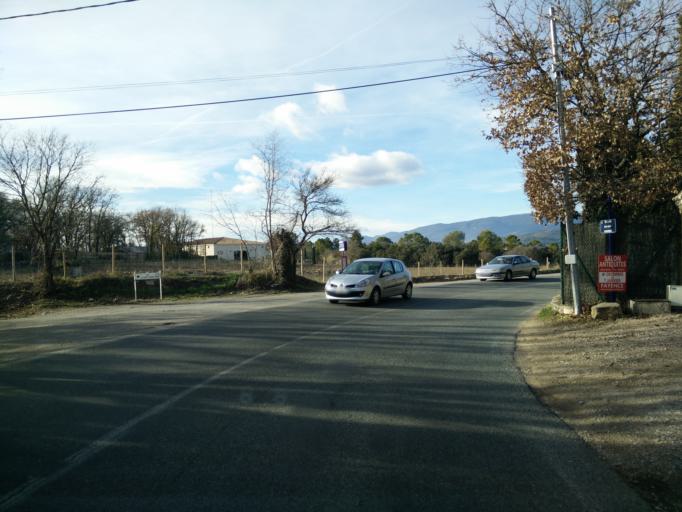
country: FR
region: Provence-Alpes-Cote d'Azur
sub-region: Departement du Var
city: Montauroux
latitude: 43.5958
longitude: 6.7885
